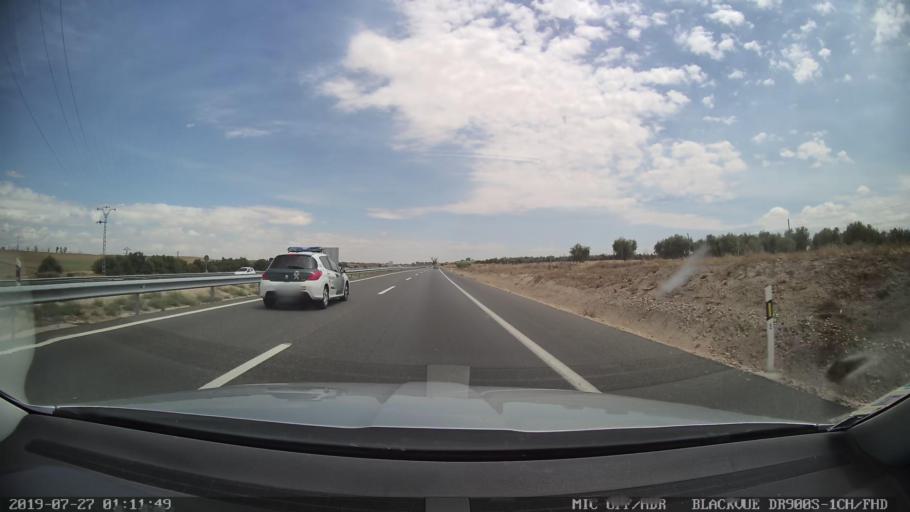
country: ES
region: Castille-La Mancha
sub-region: Province of Toledo
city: Otero
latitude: 40.0212
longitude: -4.4771
